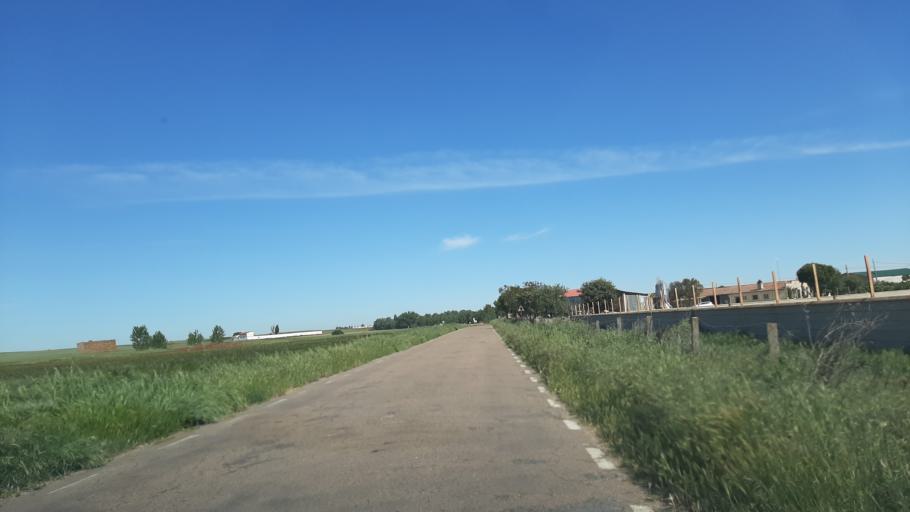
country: ES
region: Castille and Leon
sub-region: Provincia de Salamanca
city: Pedrosillo de Alba
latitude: 40.8217
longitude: -5.3974
